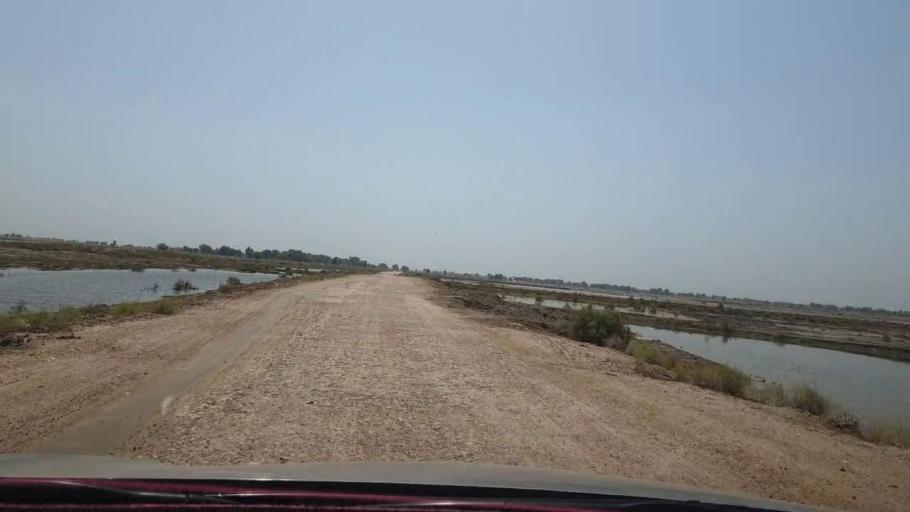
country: PK
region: Sindh
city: Kambar
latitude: 27.5773
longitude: 67.8786
